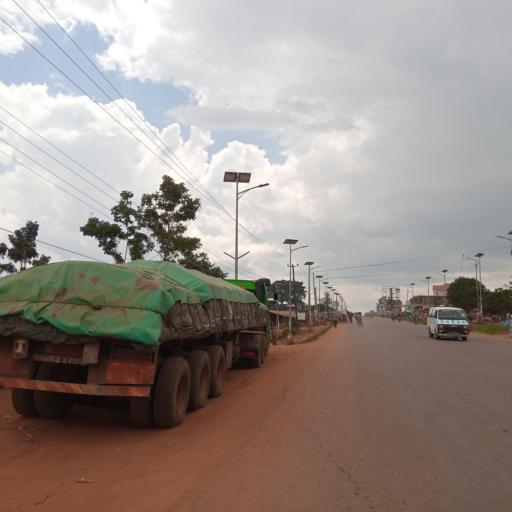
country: UG
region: Eastern Region
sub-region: Mbale District
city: Mbale
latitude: 1.0945
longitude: 34.1761
